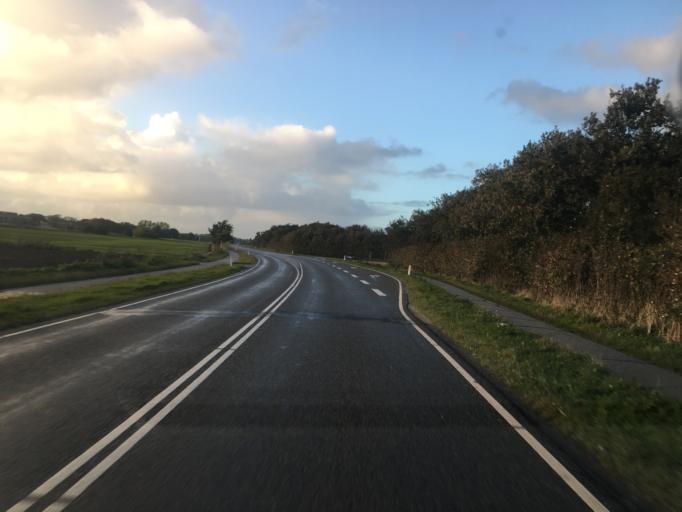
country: DK
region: South Denmark
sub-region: Tonder Kommune
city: Tonder
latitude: 54.9287
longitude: 8.8501
